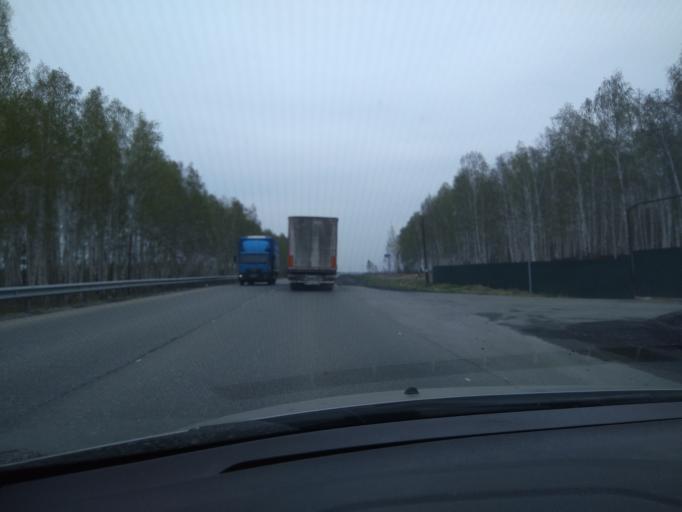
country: RU
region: Sverdlovsk
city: Zarechnyy
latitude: 56.7409
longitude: 61.2312
